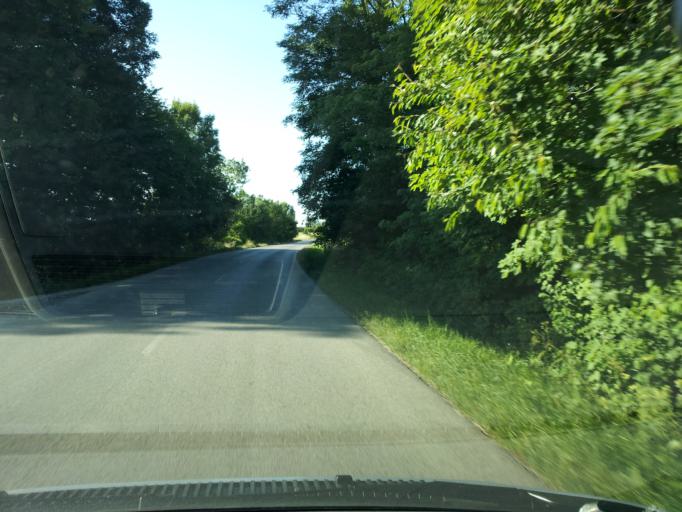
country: HU
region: Veszprem
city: Zirc
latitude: 47.2414
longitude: 17.8578
